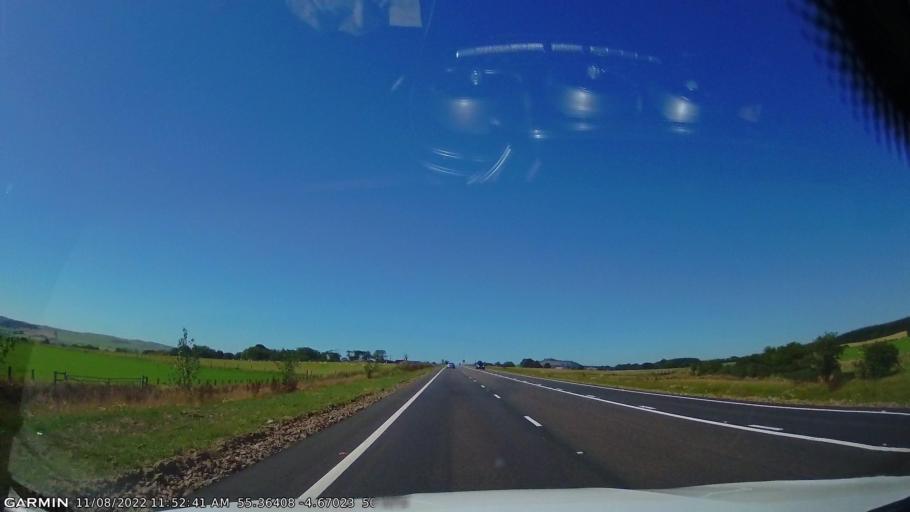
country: GB
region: Scotland
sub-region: South Ayrshire
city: Maybole
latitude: 55.3643
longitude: -4.6699
